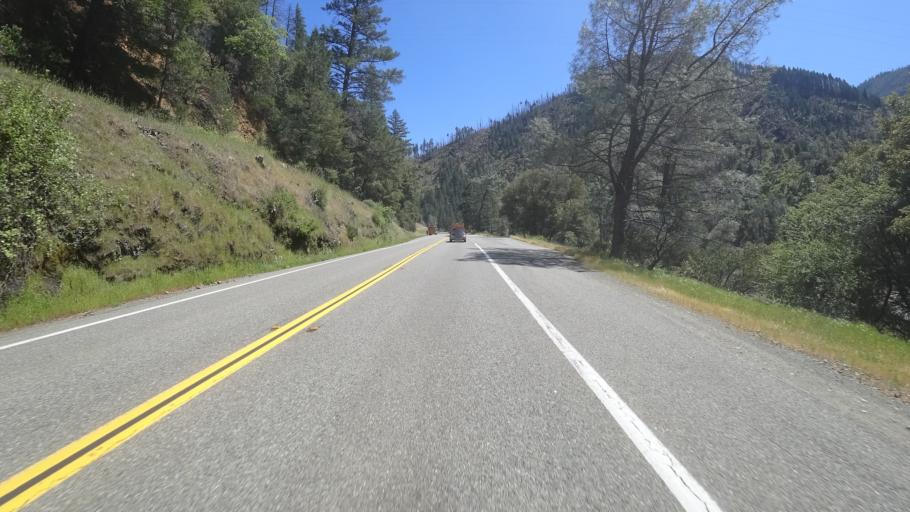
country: US
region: California
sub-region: Trinity County
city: Weaverville
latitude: 40.7695
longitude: -123.1339
